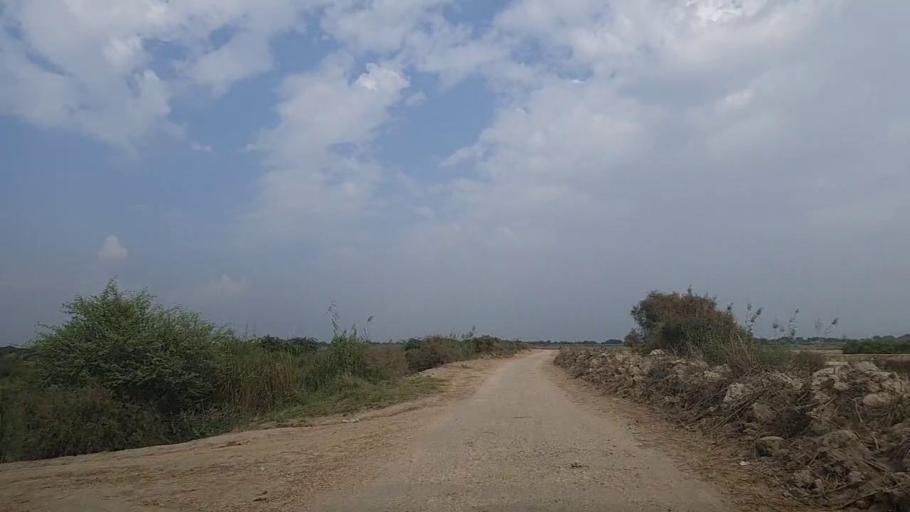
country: PK
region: Sindh
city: Daro Mehar
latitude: 24.7088
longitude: 68.1487
